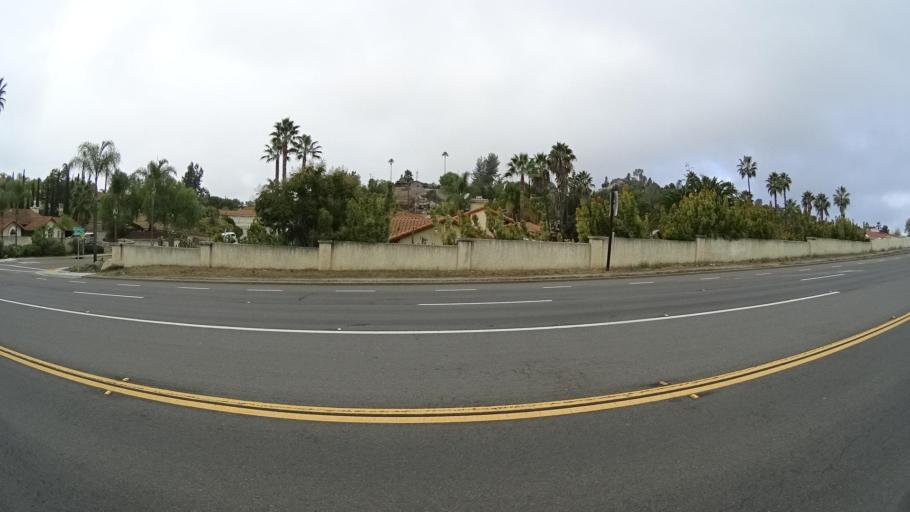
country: US
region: California
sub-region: San Diego County
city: Rancho San Diego
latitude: 32.7746
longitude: -116.9277
